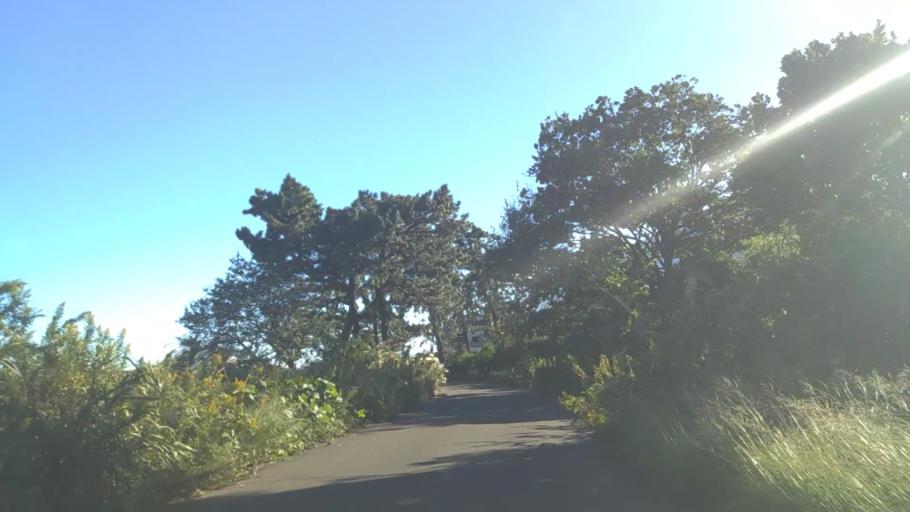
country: JP
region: Kanagawa
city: Atsugi
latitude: 35.4297
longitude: 139.3712
